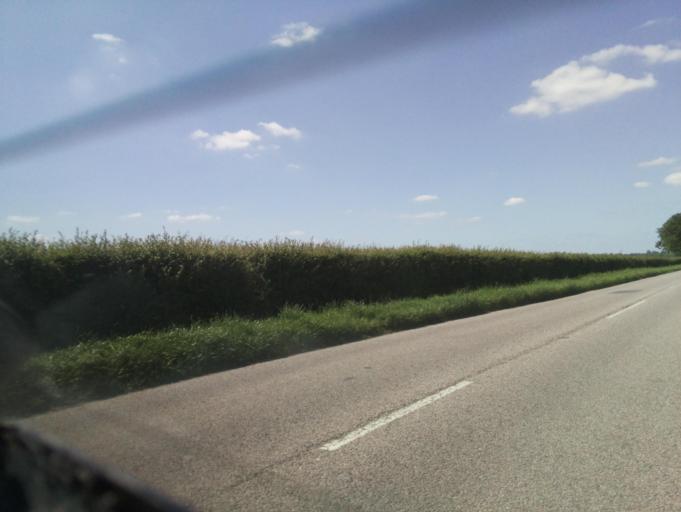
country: GB
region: England
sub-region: Borough of Swindon
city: Wroughton
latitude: 51.5330
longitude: -1.8064
